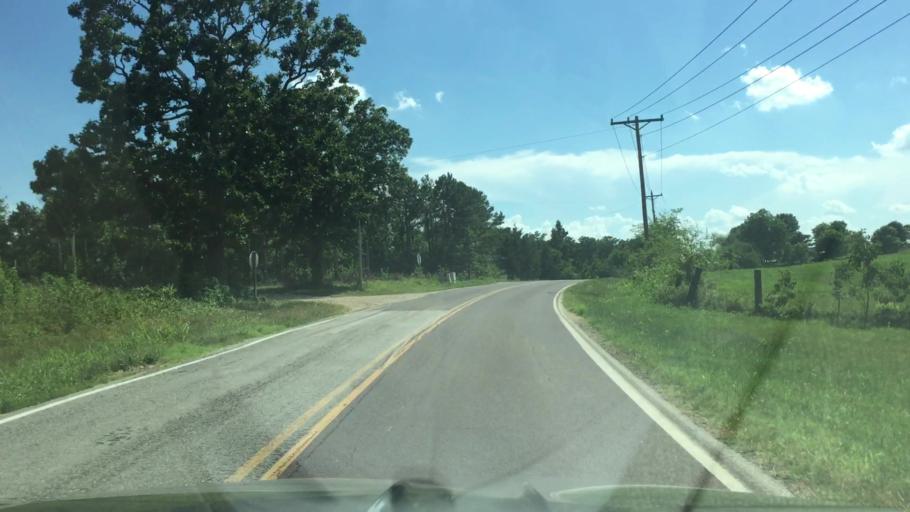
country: US
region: Missouri
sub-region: Miller County
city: Tuscumbia
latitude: 38.1259
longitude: -92.4630
